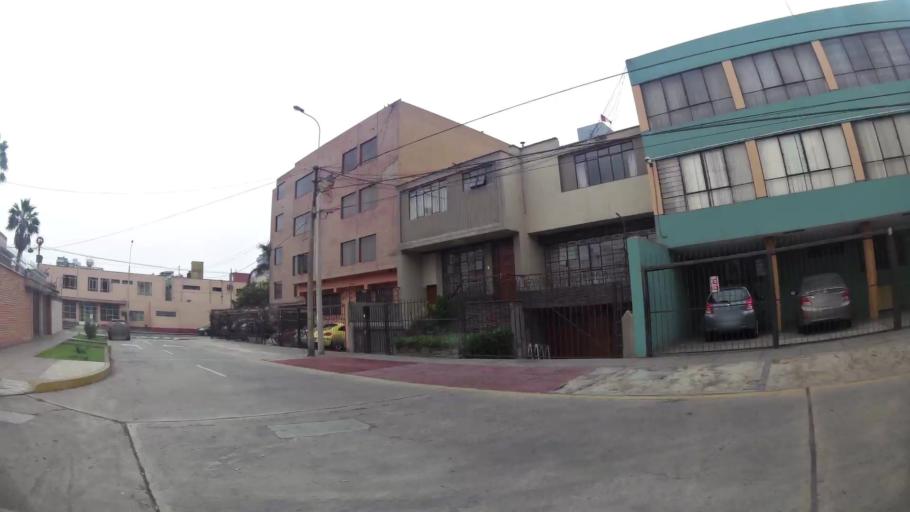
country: PE
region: Lima
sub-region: Lima
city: San Isidro
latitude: -12.1048
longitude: -77.0289
